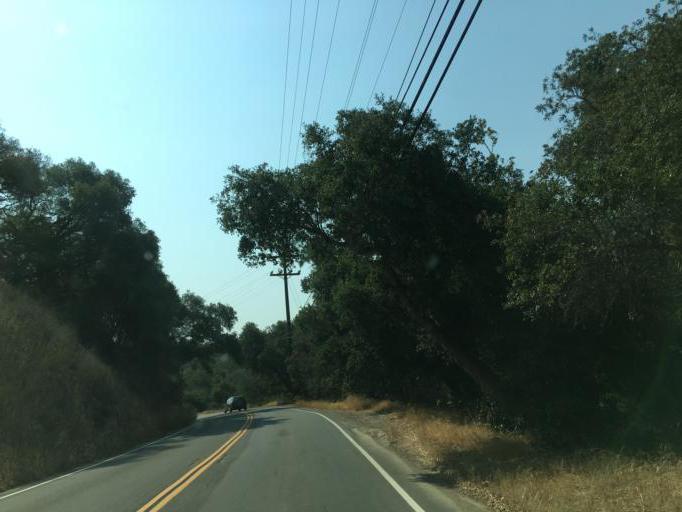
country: US
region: California
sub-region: Los Angeles County
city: Topanga
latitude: 34.0948
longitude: -118.6120
